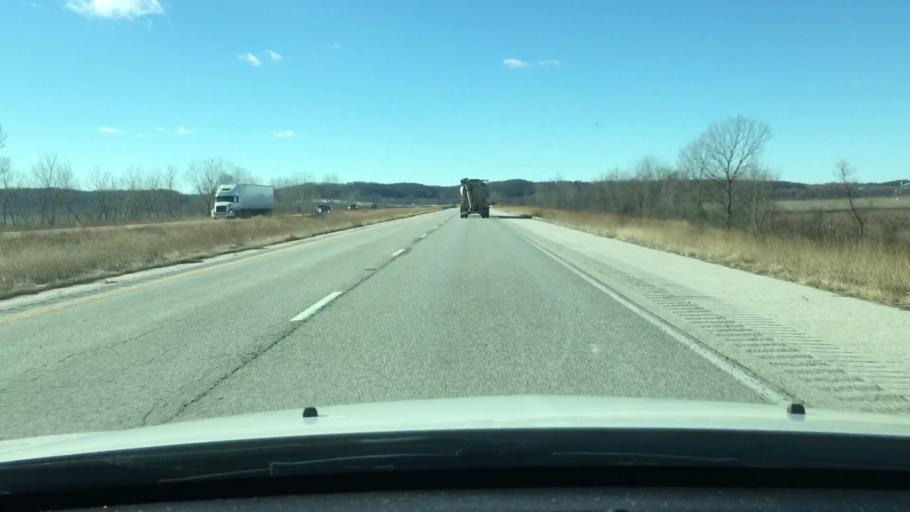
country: US
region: Illinois
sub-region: Pike County
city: Griggsville
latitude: 39.6921
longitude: -90.6151
